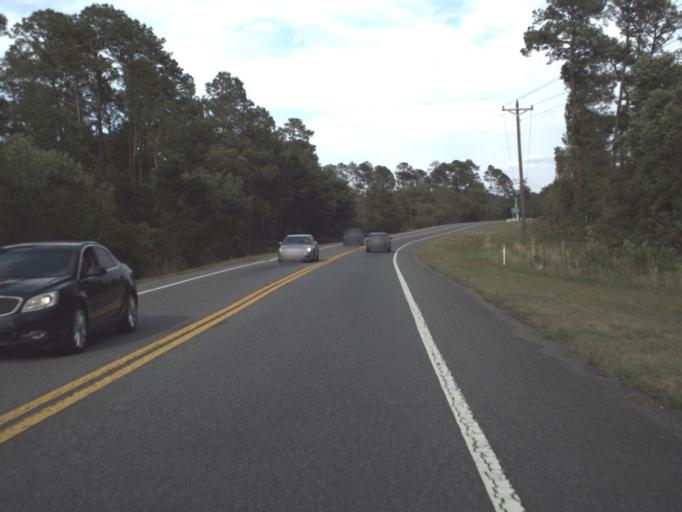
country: US
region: Florida
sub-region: Lake County
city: Astor
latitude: 29.1754
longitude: -81.6801
